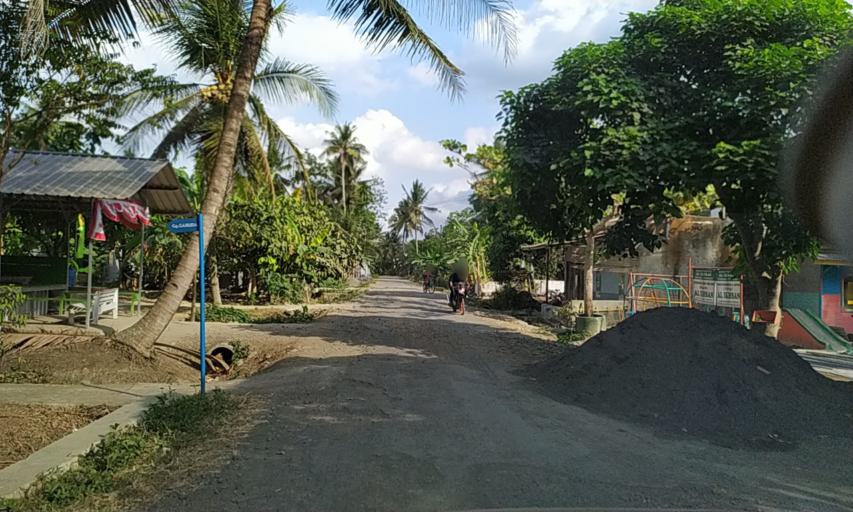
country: ID
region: Central Java
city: Gayamsari
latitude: -7.4323
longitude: 108.7264
